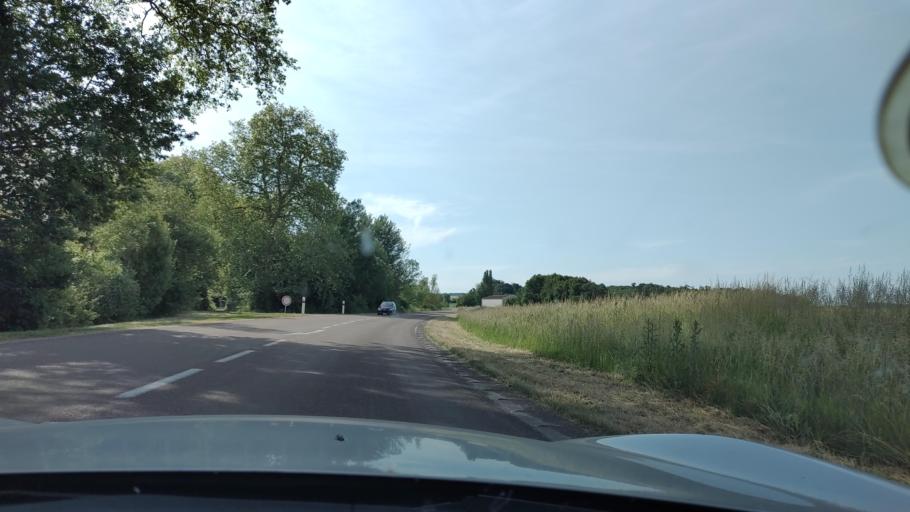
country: FR
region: Champagne-Ardenne
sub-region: Departement de l'Aube
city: Nogent-sur-Seine
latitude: 48.4702
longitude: 3.5639
